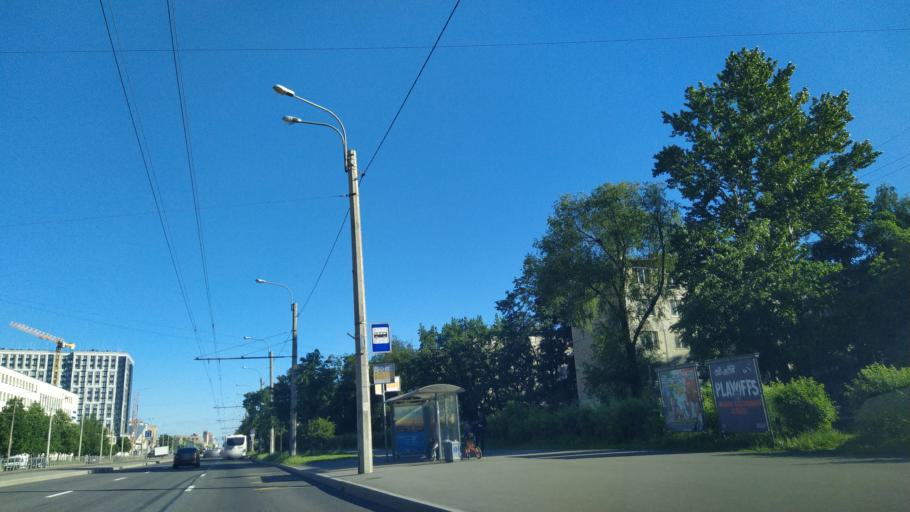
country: RU
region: St.-Petersburg
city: Kupchino
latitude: 59.8877
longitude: 30.3630
